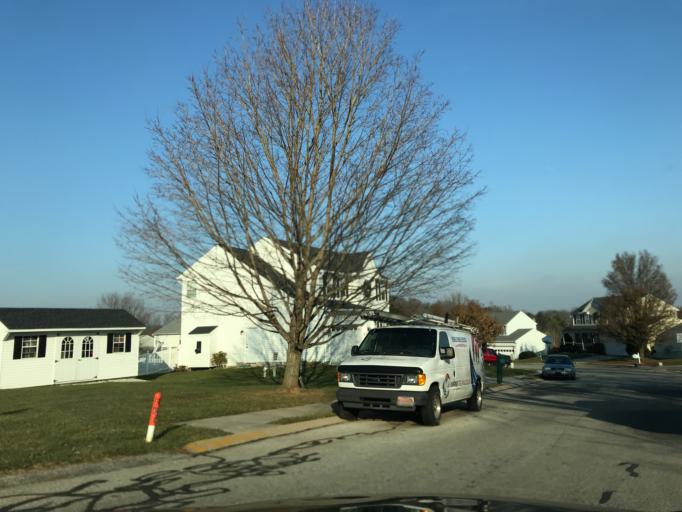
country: US
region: Pennsylvania
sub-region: York County
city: New Freedom
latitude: 39.7453
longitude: -76.7019
